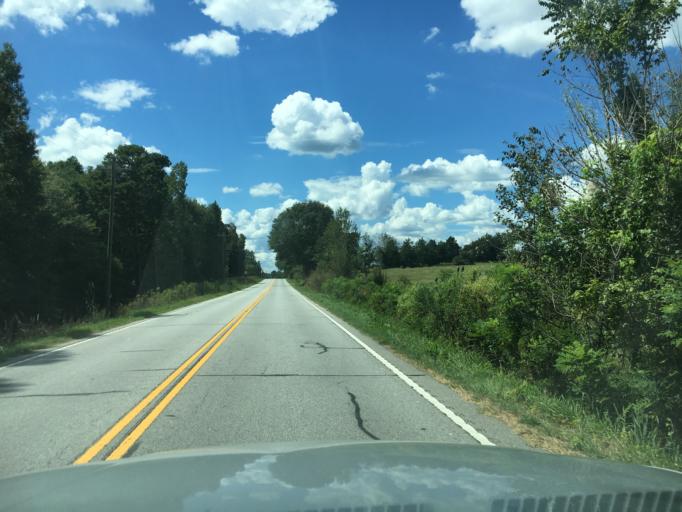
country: US
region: South Carolina
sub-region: Greenwood County
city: Ware Shoals
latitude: 34.5192
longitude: -82.1683
